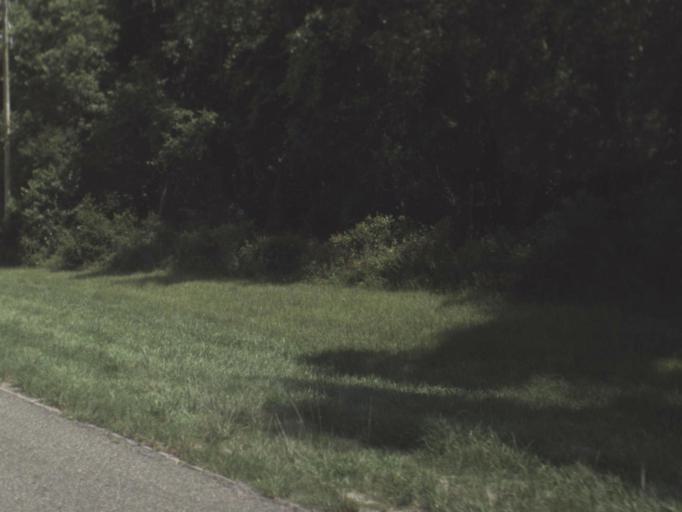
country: US
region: Florida
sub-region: Lafayette County
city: Mayo
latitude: 30.0329
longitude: -83.0628
